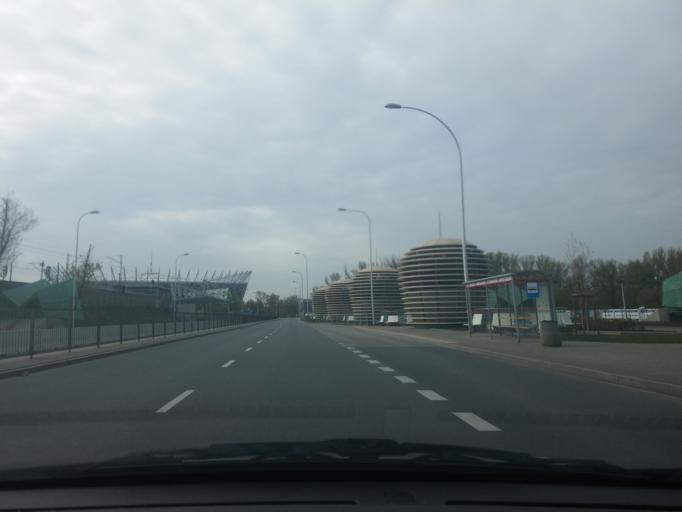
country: PL
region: Masovian Voivodeship
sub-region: Warszawa
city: Praga Polnoc
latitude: 52.2476
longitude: 21.0432
